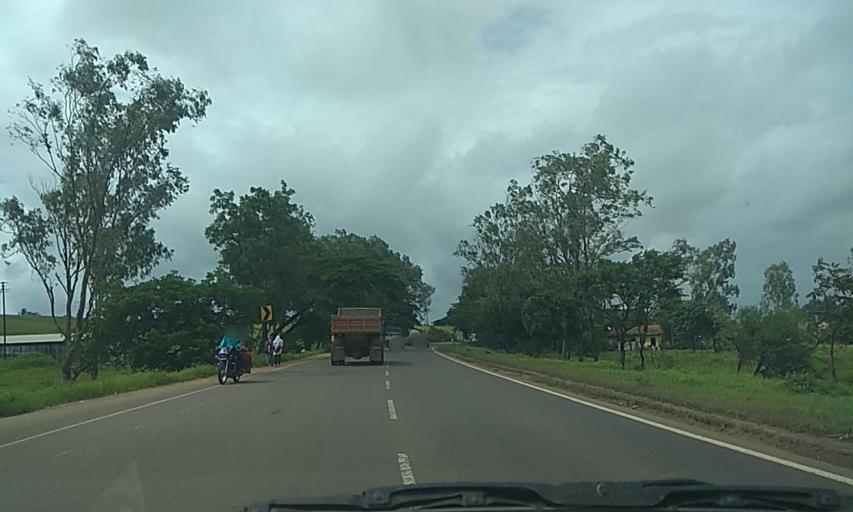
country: IN
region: Maharashtra
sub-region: Kolhapur
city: Kolhapur
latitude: 16.6567
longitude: 74.2676
